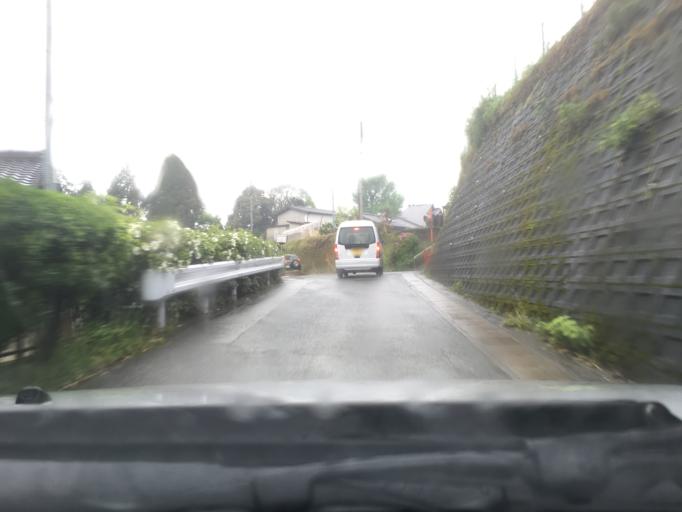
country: JP
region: Kumamoto
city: Ueki
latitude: 32.8720
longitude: 130.7002
